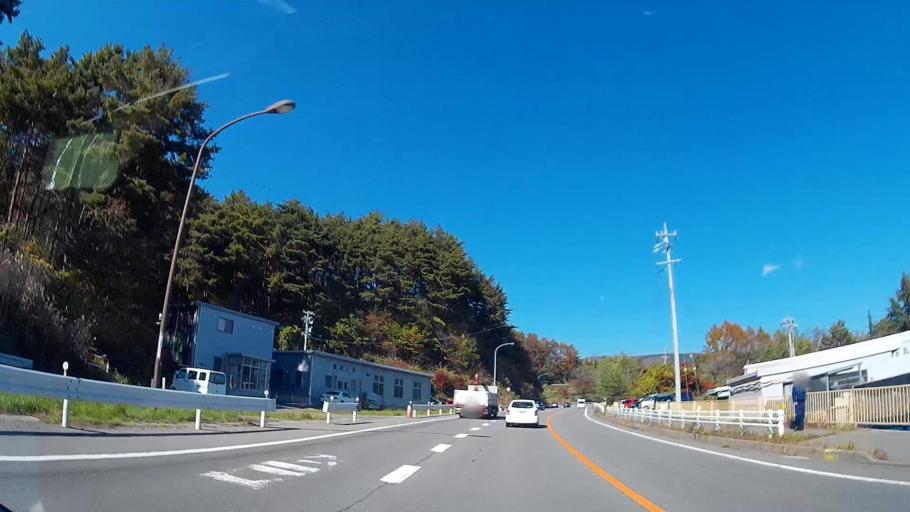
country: JP
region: Nagano
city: Okaya
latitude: 36.0771
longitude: 138.0313
